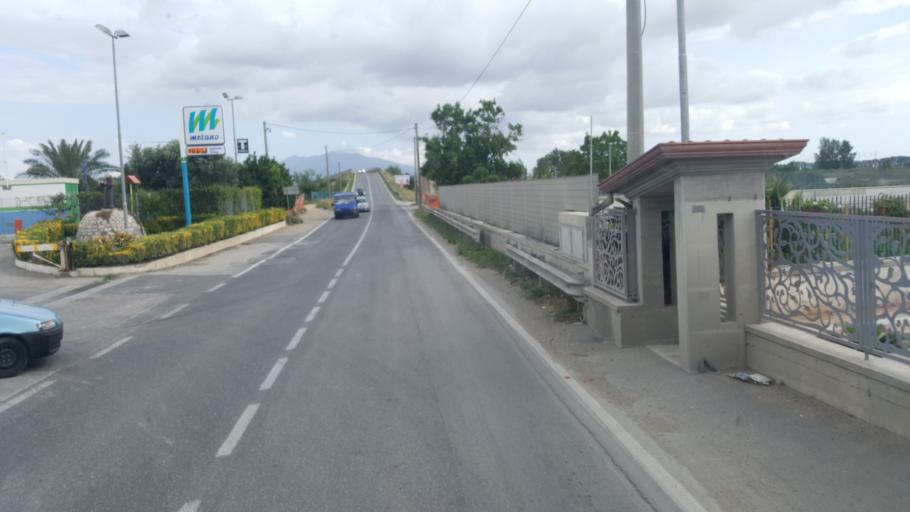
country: IT
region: Campania
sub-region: Provincia di Caserta
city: Maddaloni
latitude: 41.0051
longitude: 14.3931
